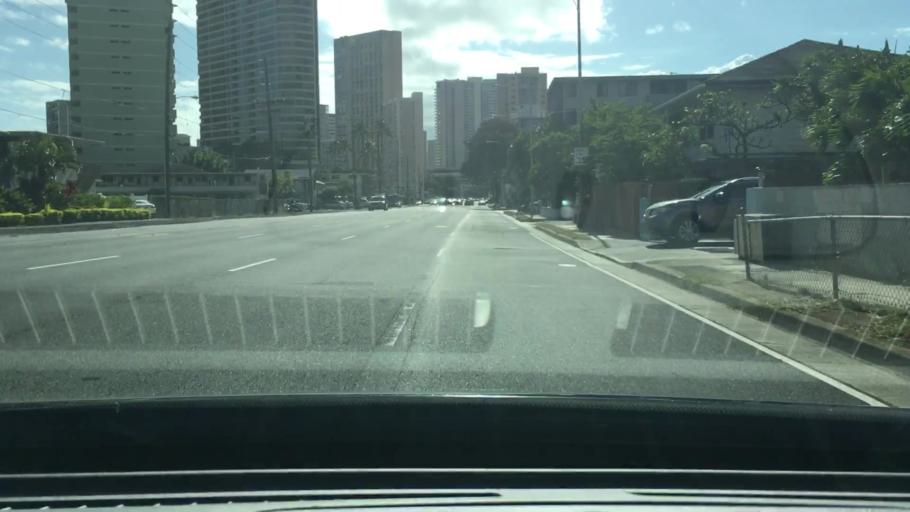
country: US
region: Hawaii
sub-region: Honolulu County
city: Honolulu
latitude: 21.2877
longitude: -157.8209
